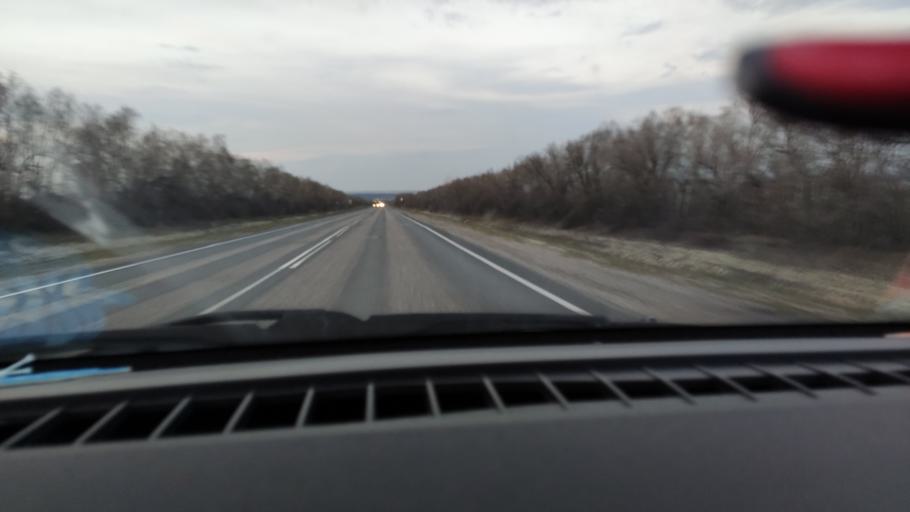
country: RU
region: Saratov
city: Sinodskoye
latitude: 51.9484
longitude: 46.6056
